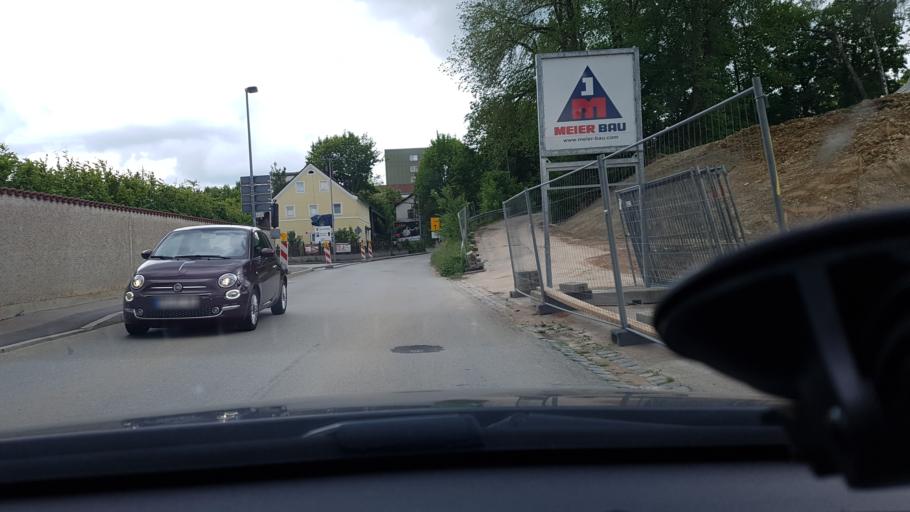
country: DE
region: Bavaria
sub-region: Lower Bavaria
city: Rotthalmunster
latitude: 48.3569
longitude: 13.2021
